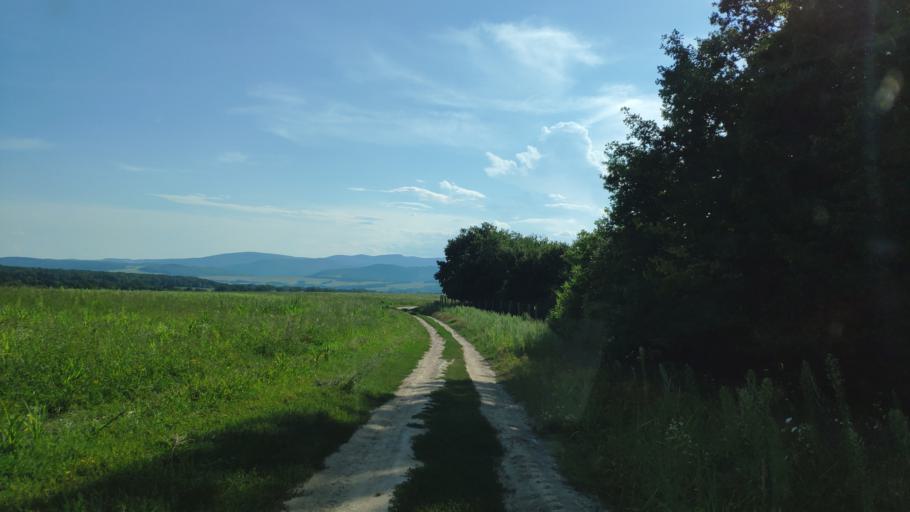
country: SK
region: Presovsky
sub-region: Okres Presov
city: Presov
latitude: 48.9167
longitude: 21.2865
